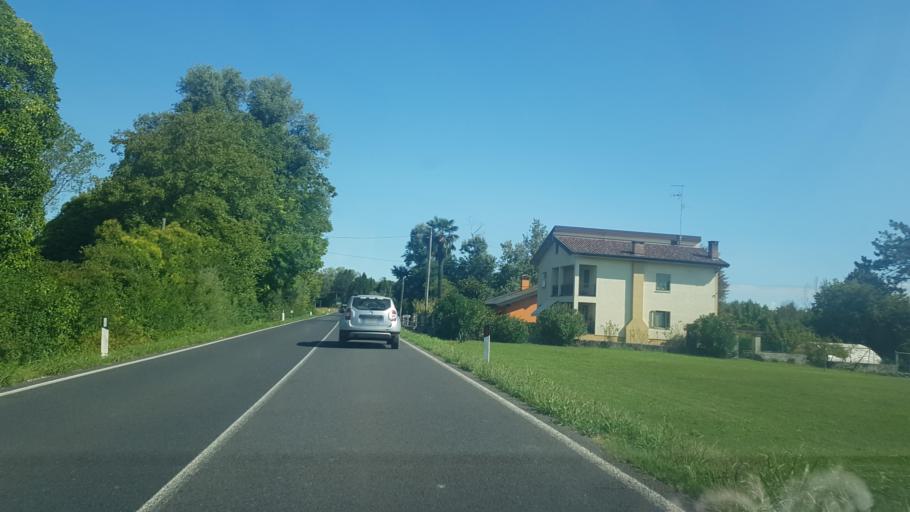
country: IT
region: Friuli Venezia Giulia
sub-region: Provincia di Udine
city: Porpetto
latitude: 45.8760
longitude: 13.2268
